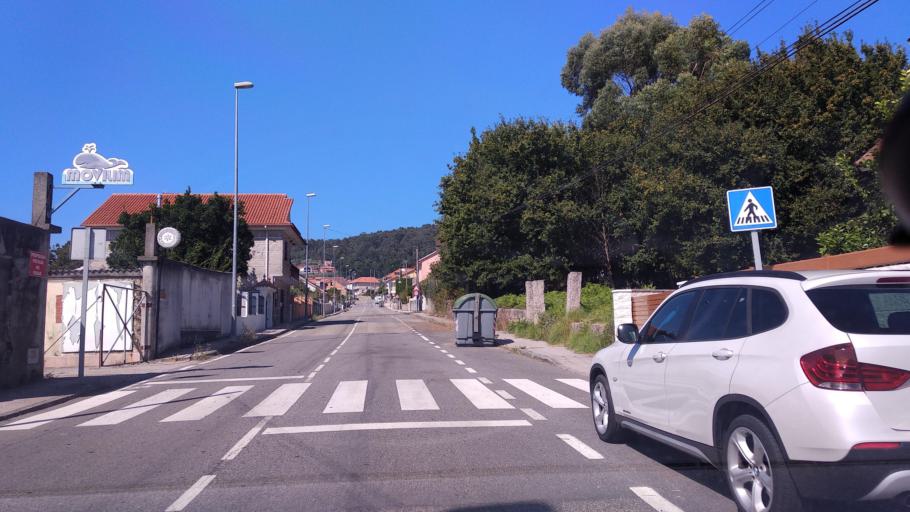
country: ES
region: Galicia
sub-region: Provincia de Pontevedra
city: Cangas
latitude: 42.2725
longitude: -8.7676
